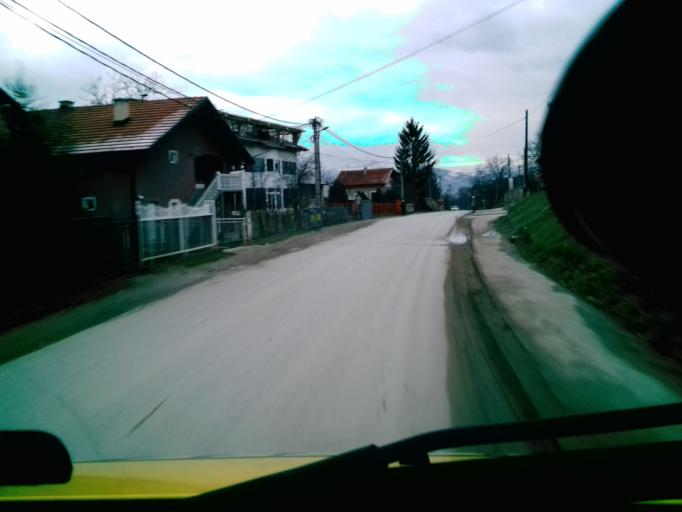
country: BA
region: Federation of Bosnia and Herzegovina
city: Zenica
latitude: 44.1867
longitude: 17.9642
